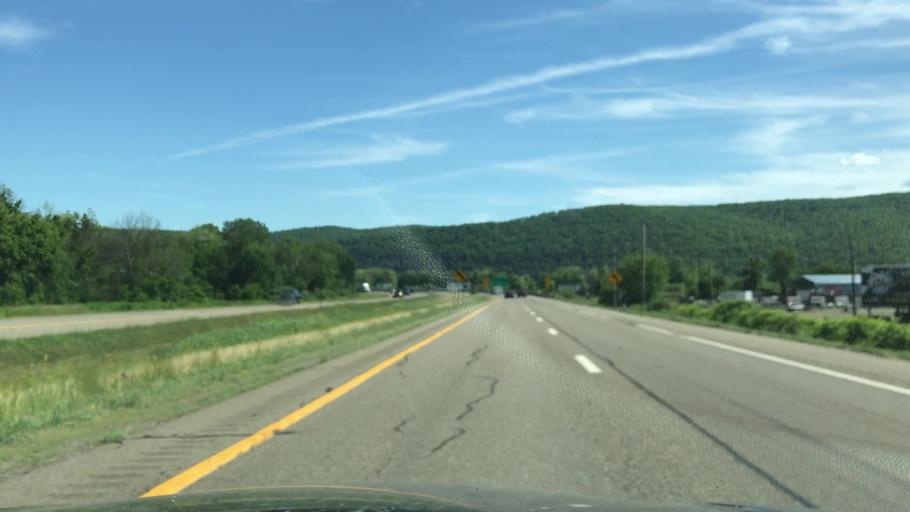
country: US
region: New York
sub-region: Steuben County
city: Gang Mills
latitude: 42.1931
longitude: -77.1607
